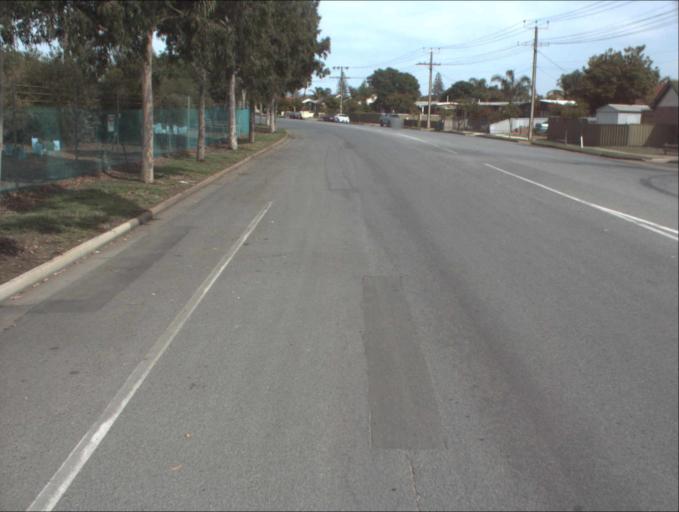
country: AU
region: South Australia
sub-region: Port Adelaide Enfield
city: Birkenhead
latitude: -34.8171
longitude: 138.5068
